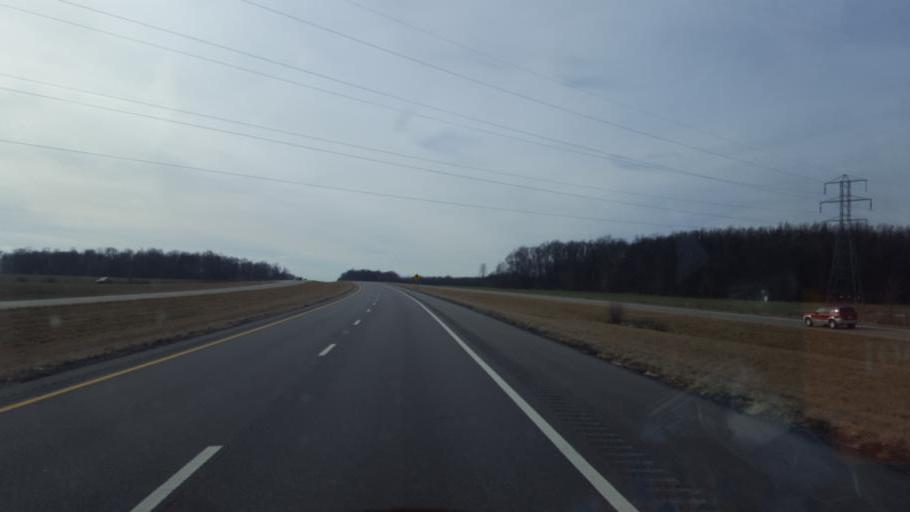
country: US
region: Ohio
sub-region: Wayne County
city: Smithville
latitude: 40.8095
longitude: -81.8477
